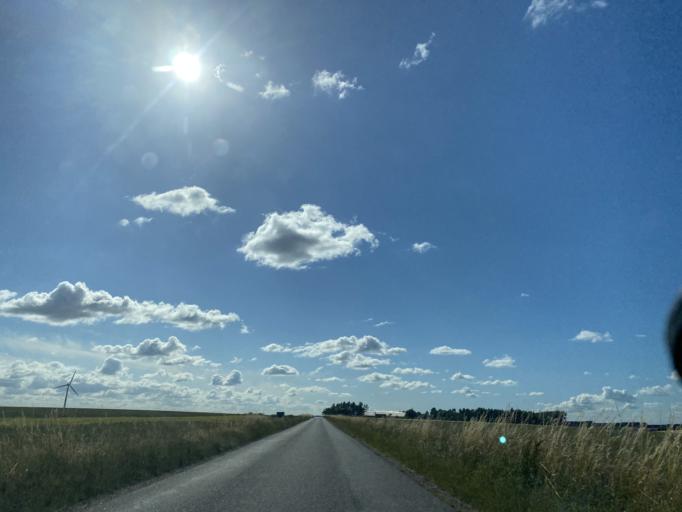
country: DK
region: Central Jutland
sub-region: Viborg Kommune
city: Bjerringbro
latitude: 56.3379
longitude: 9.7089
